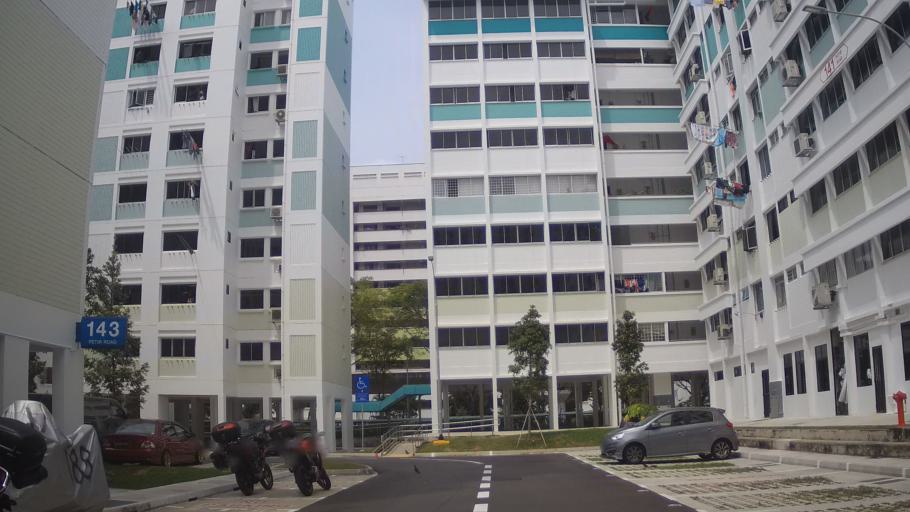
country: MY
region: Johor
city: Johor Bahru
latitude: 1.3760
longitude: 103.7684
